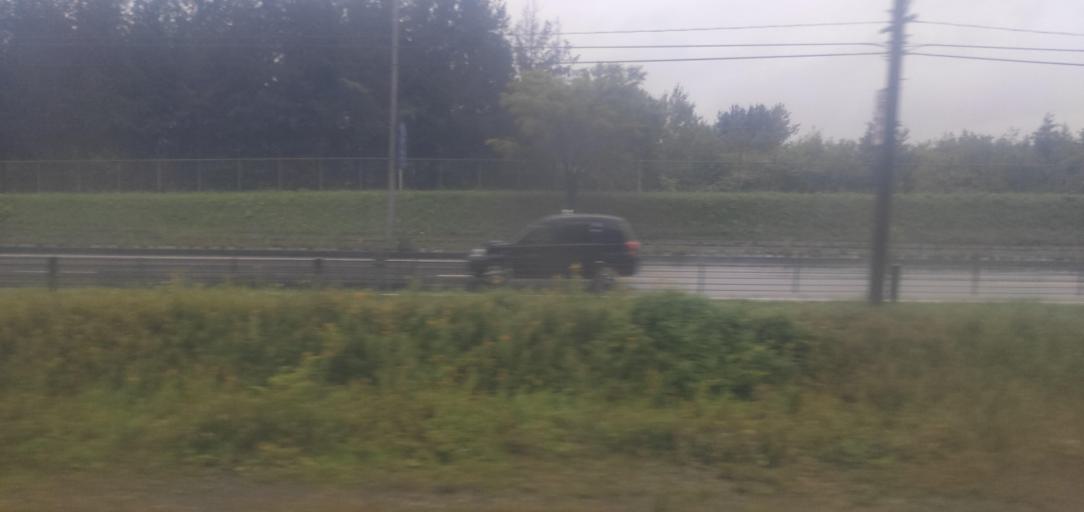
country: JP
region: Hokkaido
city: Chitose
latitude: 42.8175
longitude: 141.6641
